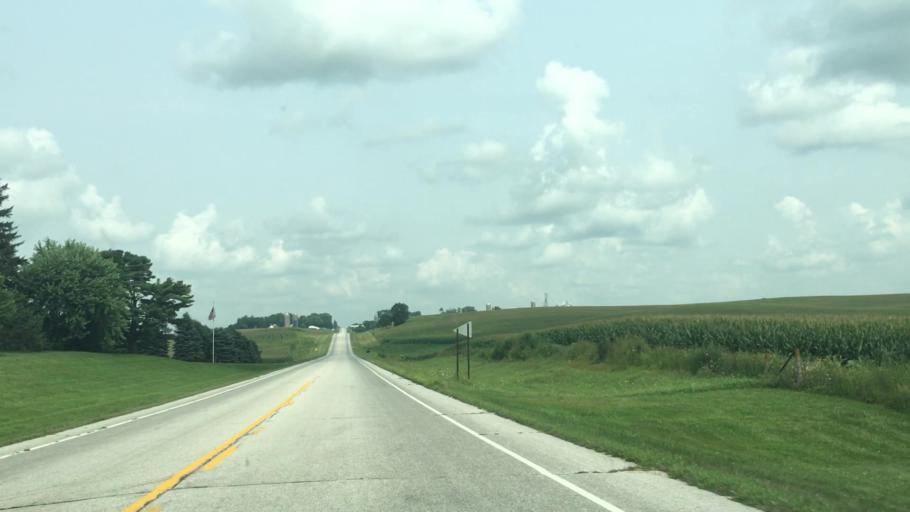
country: US
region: Minnesota
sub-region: Fillmore County
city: Harmony
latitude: 43.6036
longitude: -91.9297
